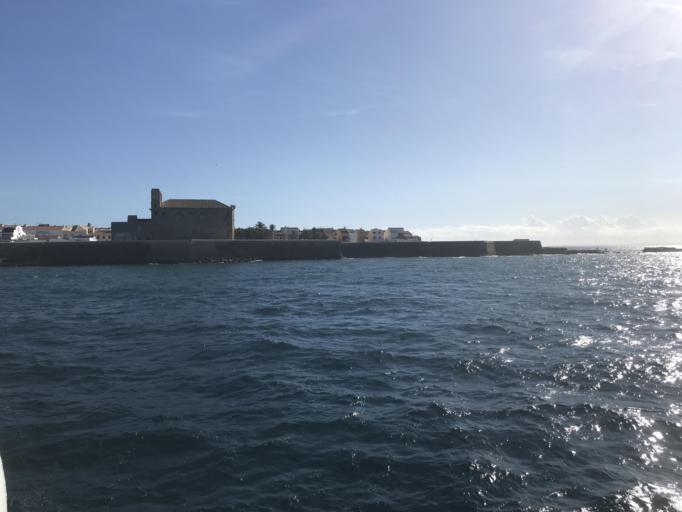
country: ES
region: Valencia
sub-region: Provincia de Alicante
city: Santa Pola
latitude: 38.1692
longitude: -0.4820
